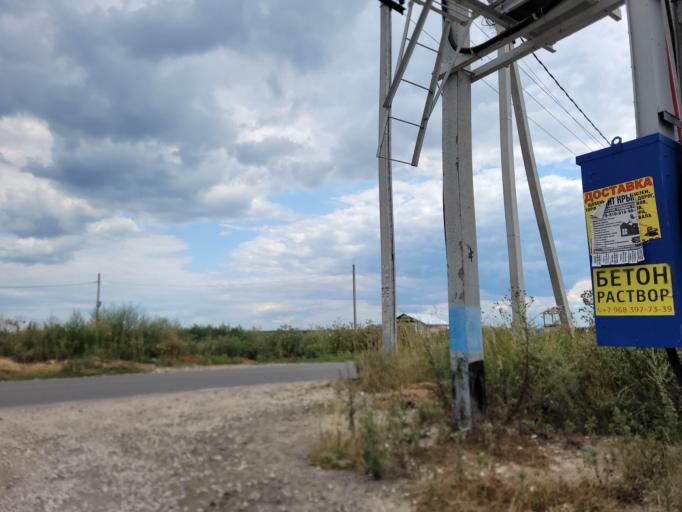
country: RU
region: Moskovskaya
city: Ramenskoye
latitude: 55.5400
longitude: 38.2314
